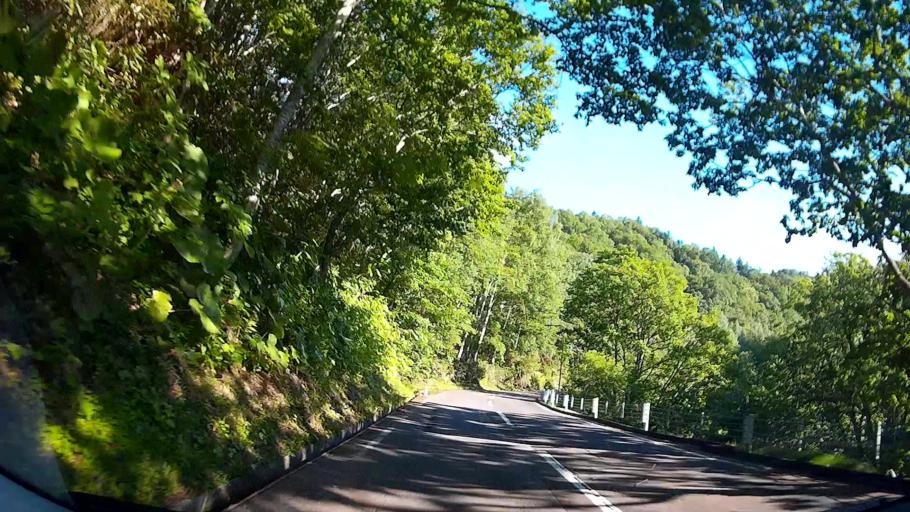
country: JP
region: Hokkaido
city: Otaru
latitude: 42.9892
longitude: 141.0769
